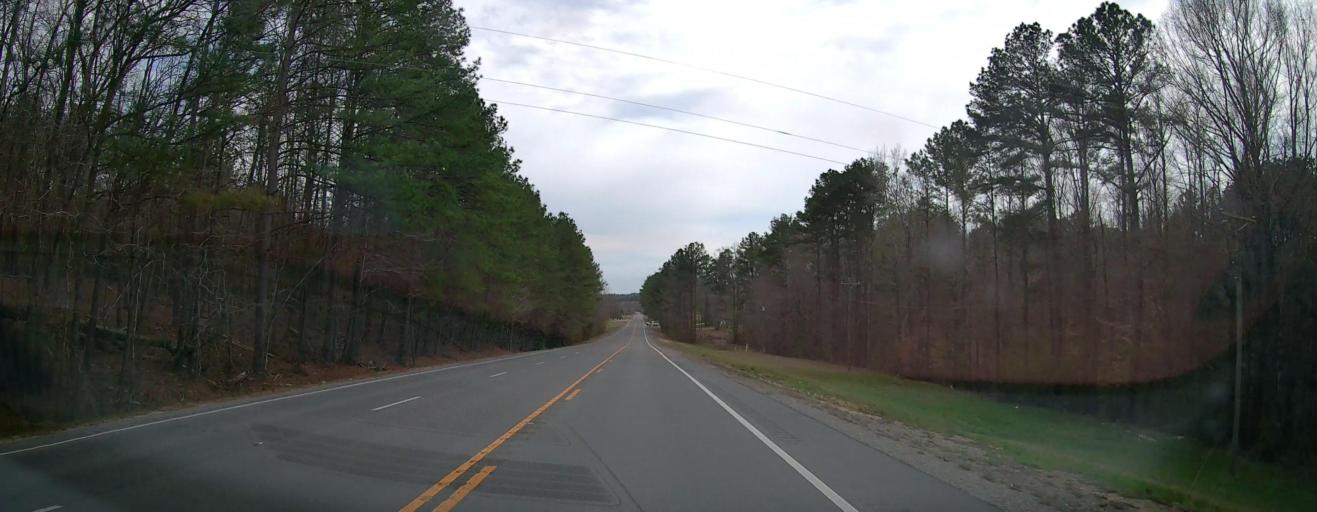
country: US
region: Alabama
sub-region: Marion County
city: Guin
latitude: 34.0149
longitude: -87.9366
